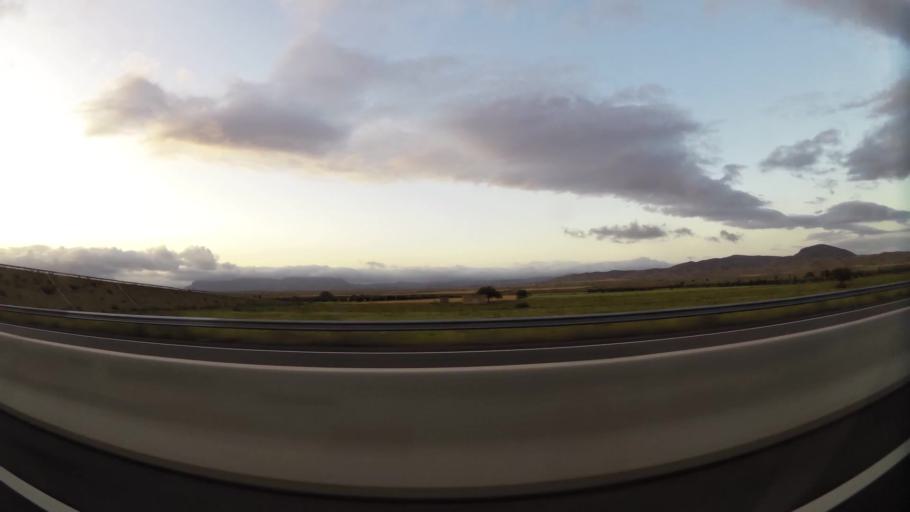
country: MA
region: Oriental
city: El Aioun
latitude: 34.5947
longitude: -2.7049
